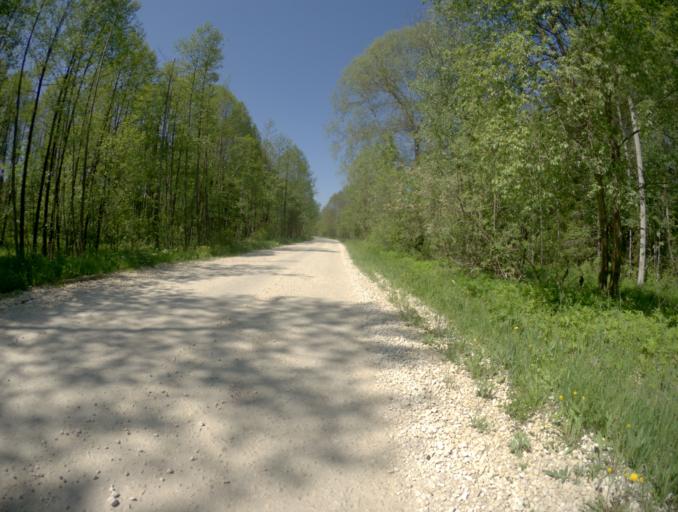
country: RU
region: Vladimir
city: Anopino
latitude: 55.7090
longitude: 40.6346
